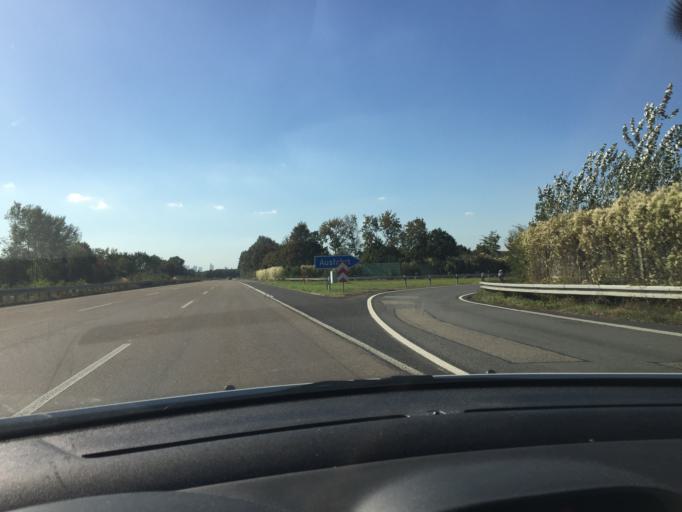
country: DE
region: Hesse
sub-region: Regierungsbezirk Darmstadt
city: Maintal
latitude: 50.1443
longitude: 8.8052
